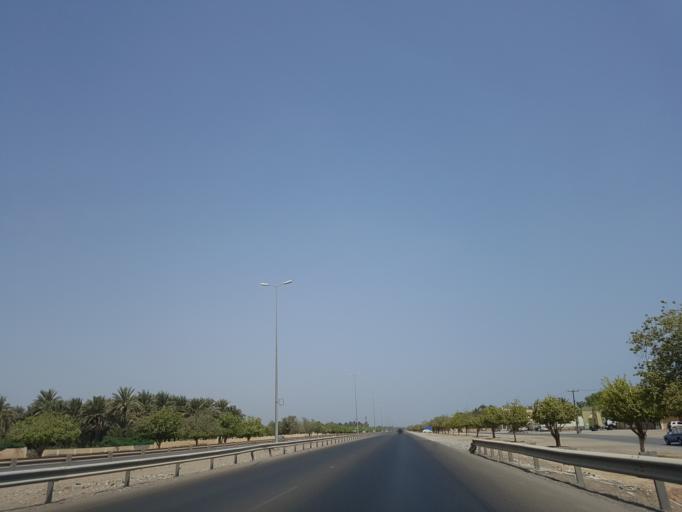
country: OM
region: Al Batinah
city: Saham
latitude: 24.1651
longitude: 56.8626
